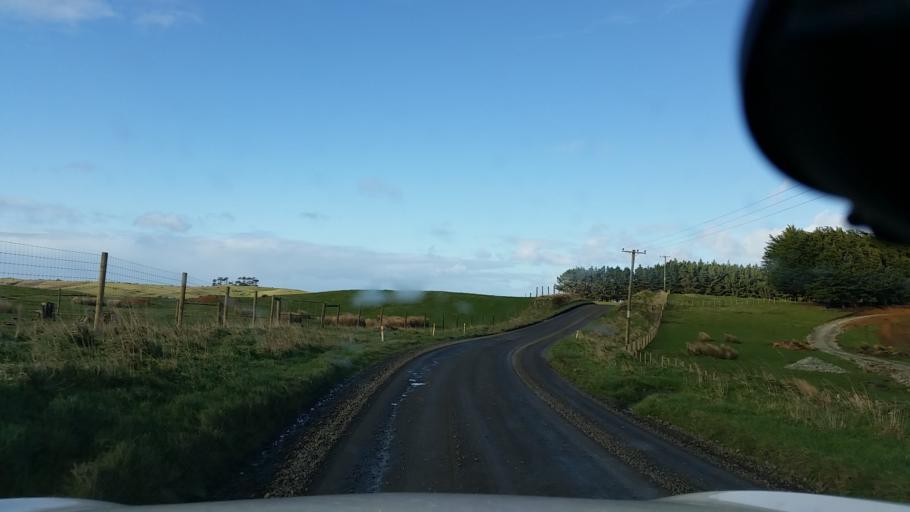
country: NZ
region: Chatham Islands
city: Waitangi
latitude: -43.9758
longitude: -176.4684
